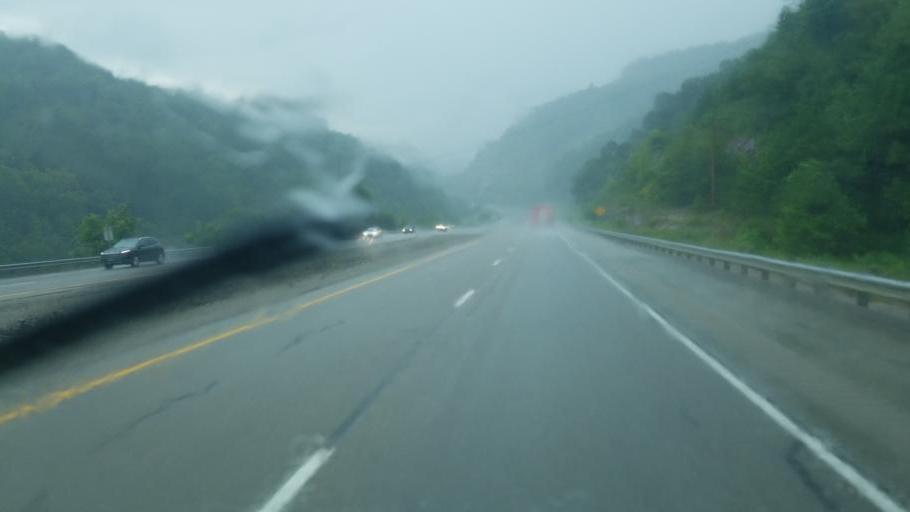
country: US
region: West Virginia
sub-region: Mingo County
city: Williamson
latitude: 37.5874
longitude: -82.3959
